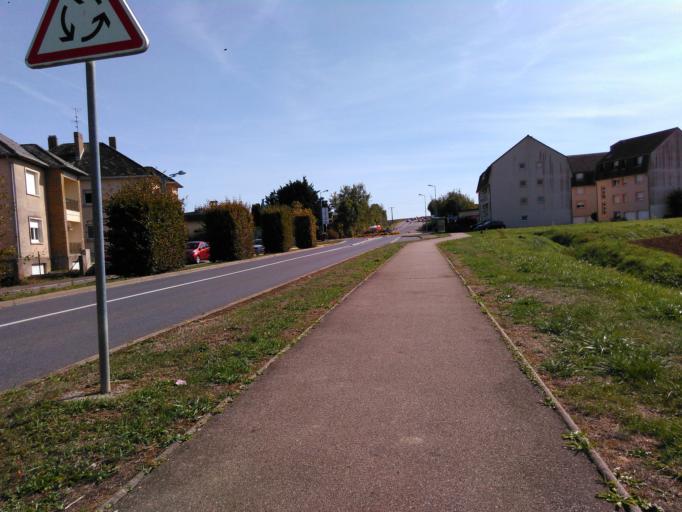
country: FR
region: Lorraine
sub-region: Departement de la Moselle
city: Hettange-Grande
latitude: 49.3945
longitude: 6.1654
